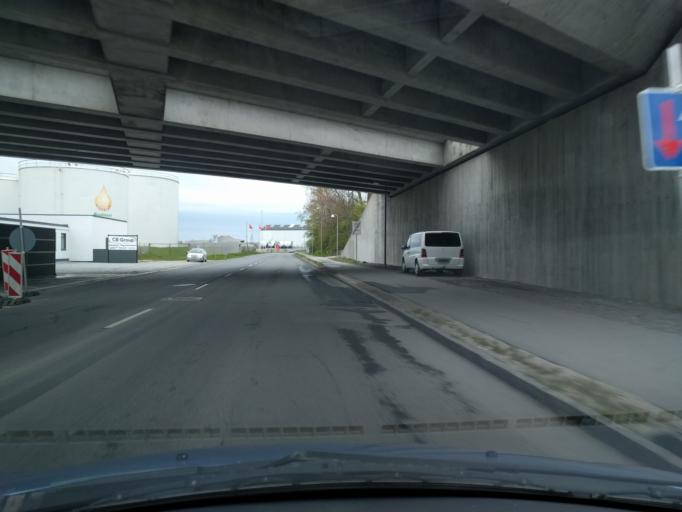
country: DK
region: South Denmark
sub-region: Odense Kommune
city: Odense
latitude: 55.4220
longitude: 10.3829
